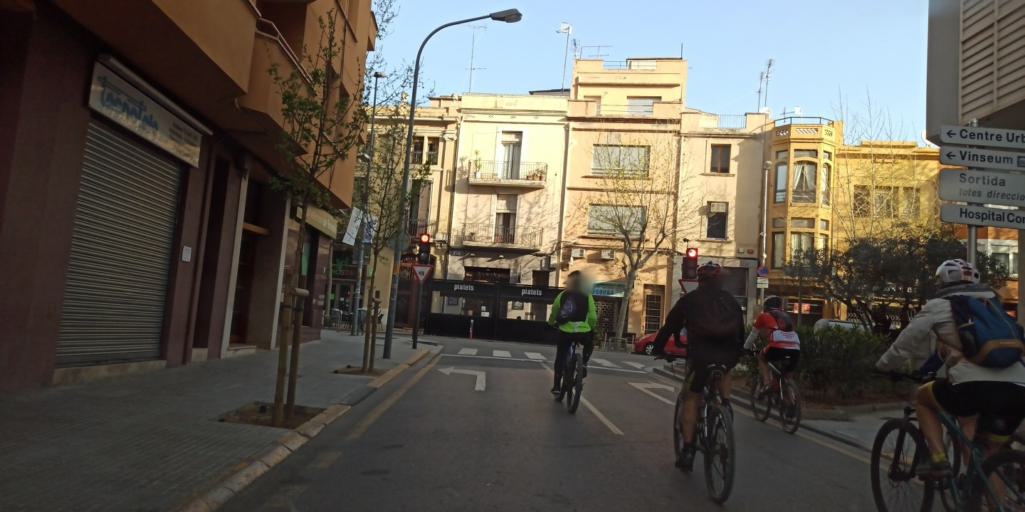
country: ES
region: Catalonia
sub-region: Provincia de Barcelona
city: Vilafranca del Penedes
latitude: 41.3458
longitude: 1.7027
